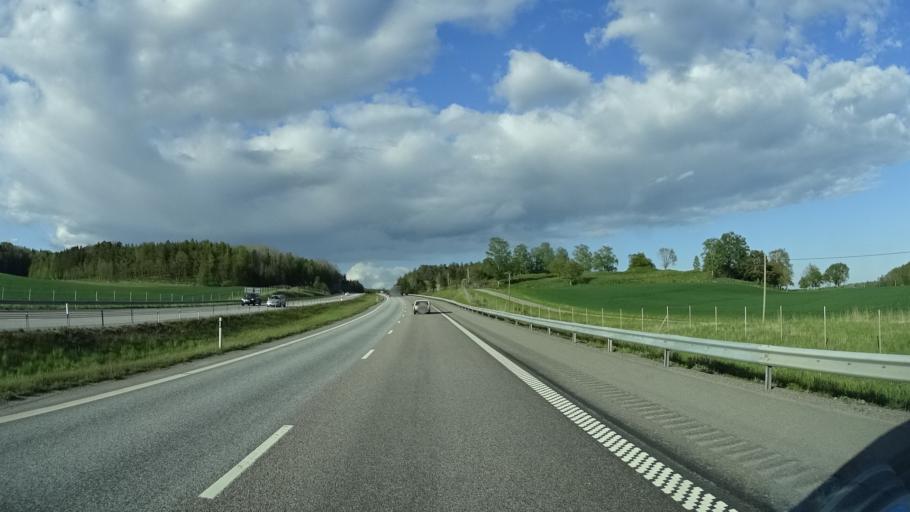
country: SE
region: Soedermanland
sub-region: Trosa Kommun
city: Vagnharad
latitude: 58.9653
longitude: 17.5016
